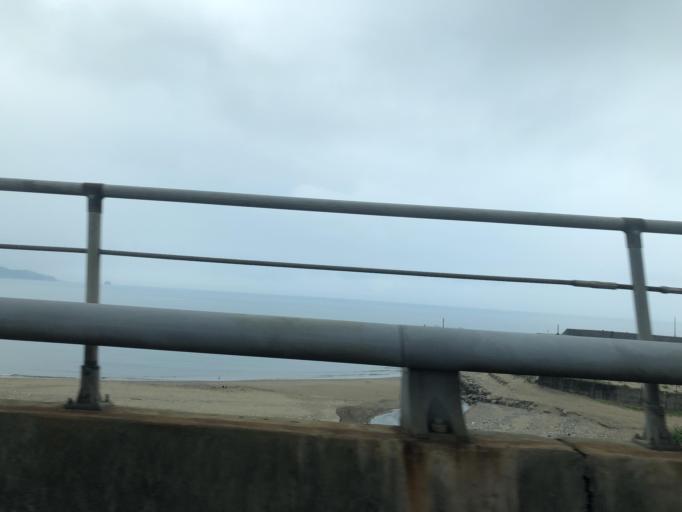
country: TW
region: Taiwan
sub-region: Keelung
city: Keelung
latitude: 25.2013
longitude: 121.6734
